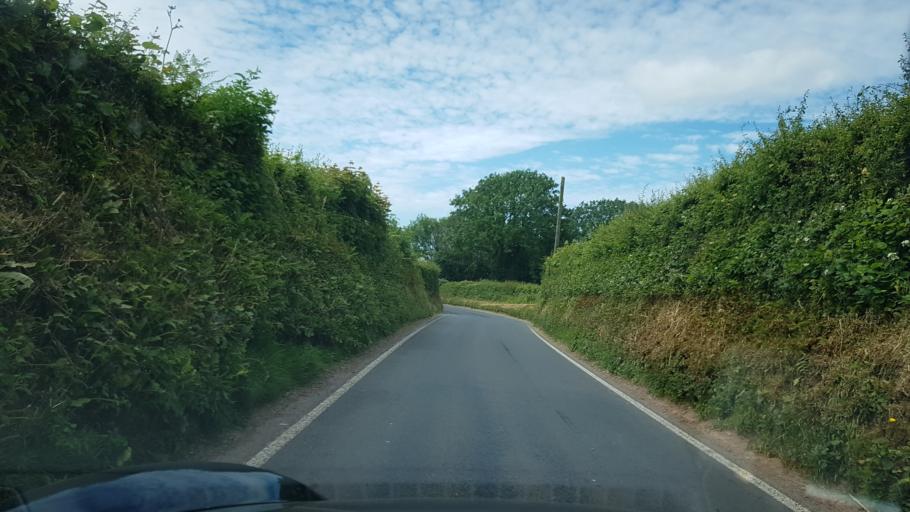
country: GB
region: Wales
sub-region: Carmarthenshire
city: Llanddowror
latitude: 51.7658
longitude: -4.5627
